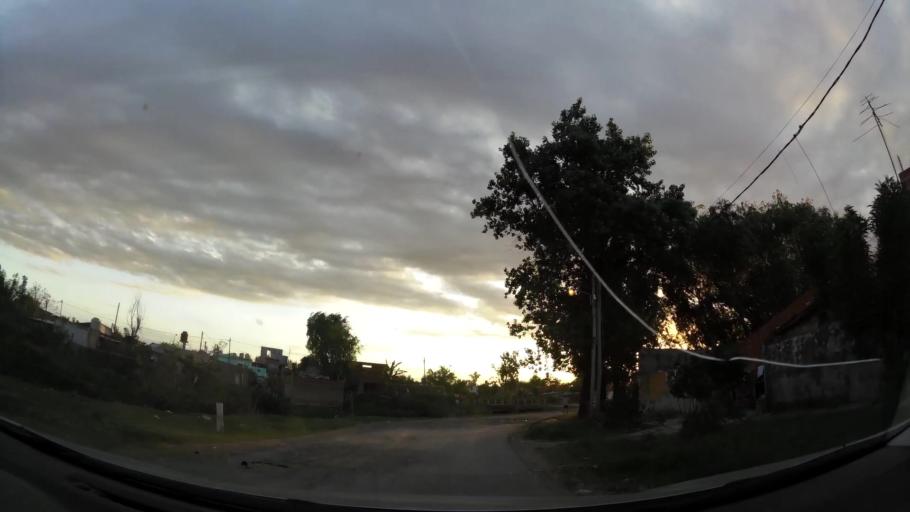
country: AR
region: Buenos Aires
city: Santa Catalina - Dique Lujan
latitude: -34.4396
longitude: -58.6620
